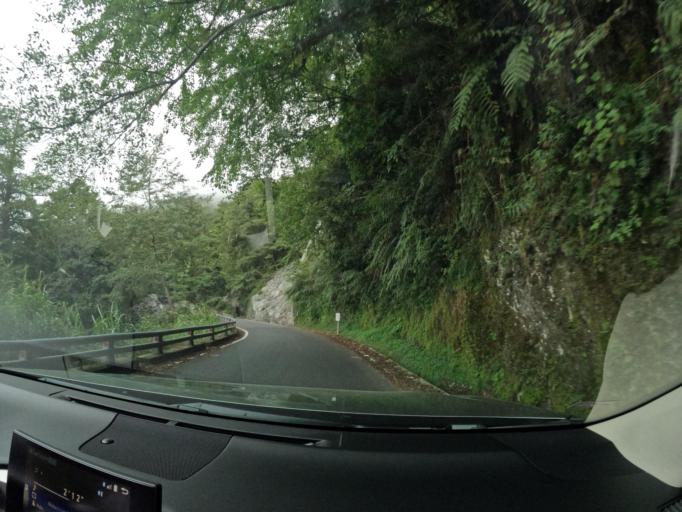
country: TW
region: Taiwan
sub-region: Taitung
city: Taitung
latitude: 23.2419
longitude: 120.9854
